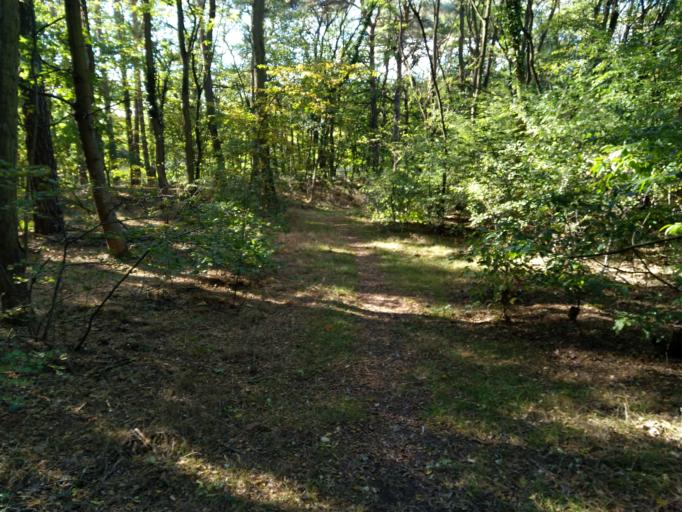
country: DE
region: Berlin
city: Rahnsdorf
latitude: 52.4417
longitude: 13.7209
